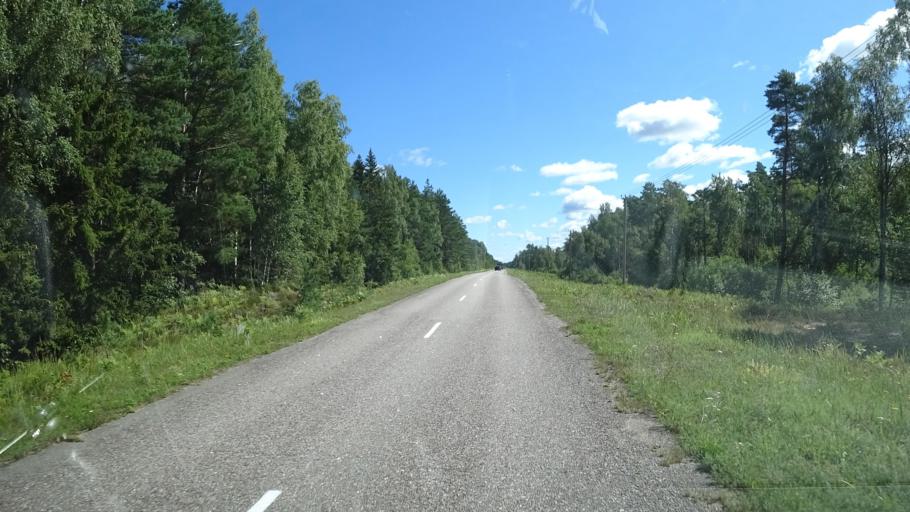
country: LV
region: Ventspils
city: Ventspils
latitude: 57.5594
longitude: 21.7867
